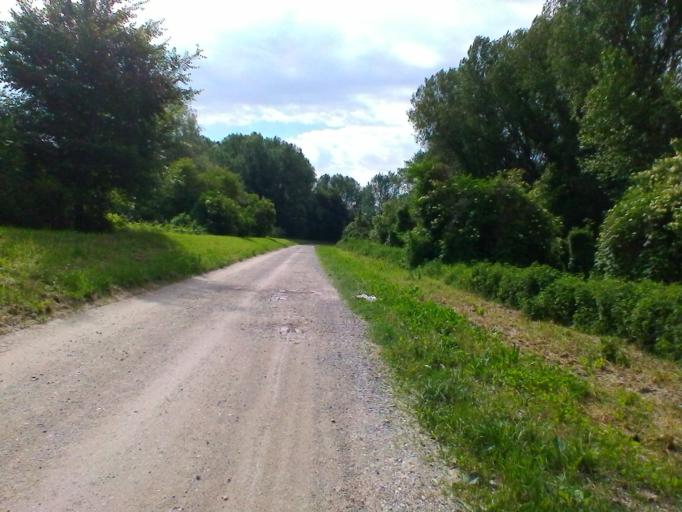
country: IT
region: Lombardy
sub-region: Provincia di Mantova
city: Cerese
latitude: 45.1340
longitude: 10.8077
